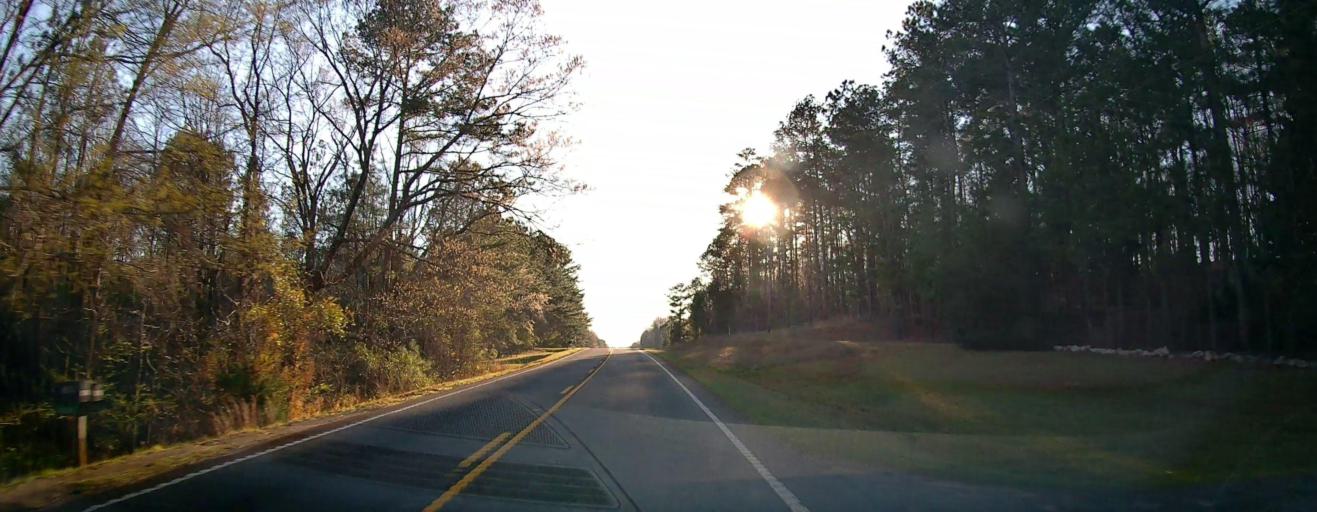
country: US
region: Georgia
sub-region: Talbot County
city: Talbotton
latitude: 32.6625
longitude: -84.6320
